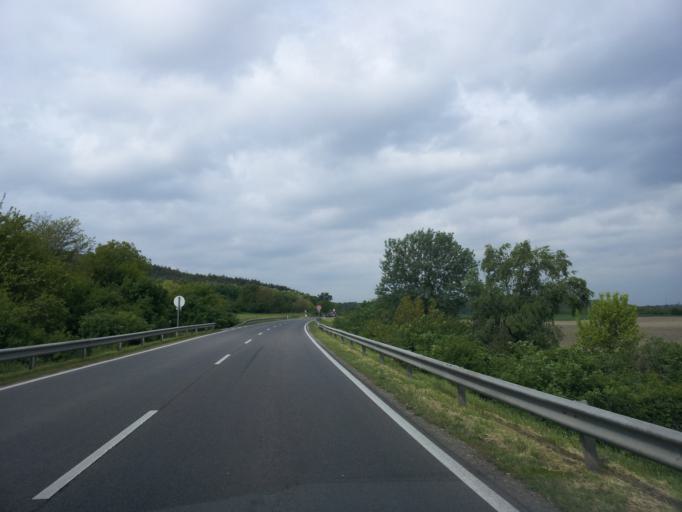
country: HU
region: Tolna
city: Szentgalpuszta
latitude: 46.3617
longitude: 18.6304
